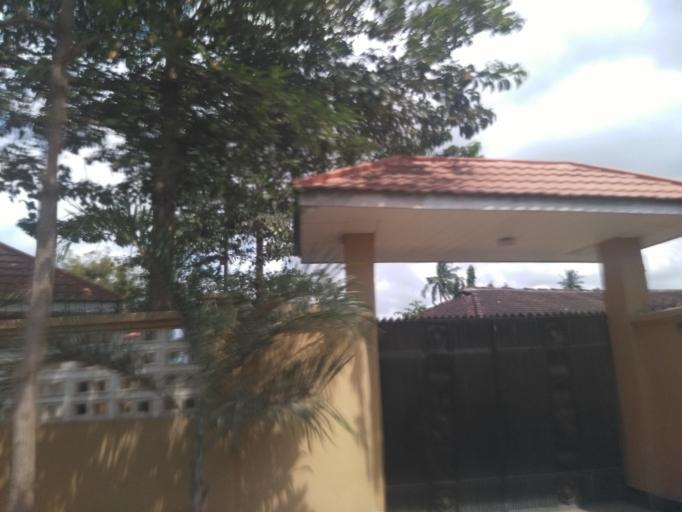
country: TZ
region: Dar es Salaam
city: Dar es Salaam
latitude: -6.8894
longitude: 39.2878
